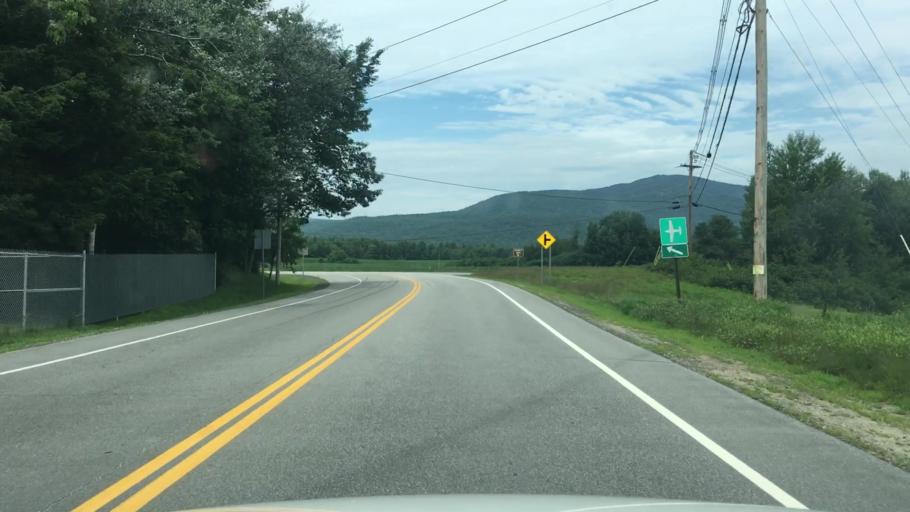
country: US
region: New Hampshire
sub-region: Grafton County
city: Plymouth
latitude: 43.7768
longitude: -71.7419
